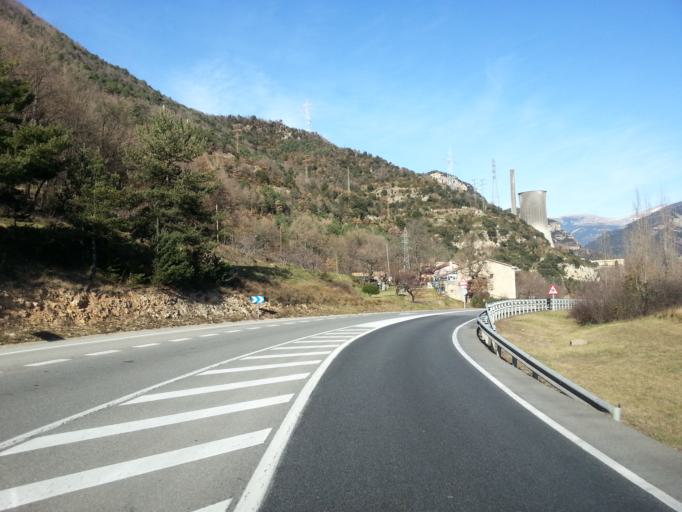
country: ES
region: Catalonia
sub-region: Provincia de Barcelona
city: Vallcebre
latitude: 42.1651
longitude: 1.8552
